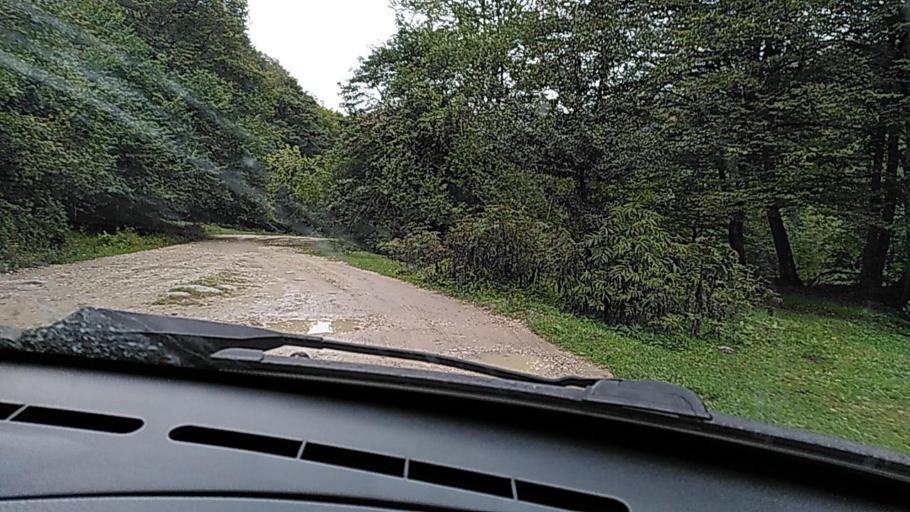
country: RU
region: Kabardino-Balkariya
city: Belaya Rechka
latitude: 43.4127
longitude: 43.4730
